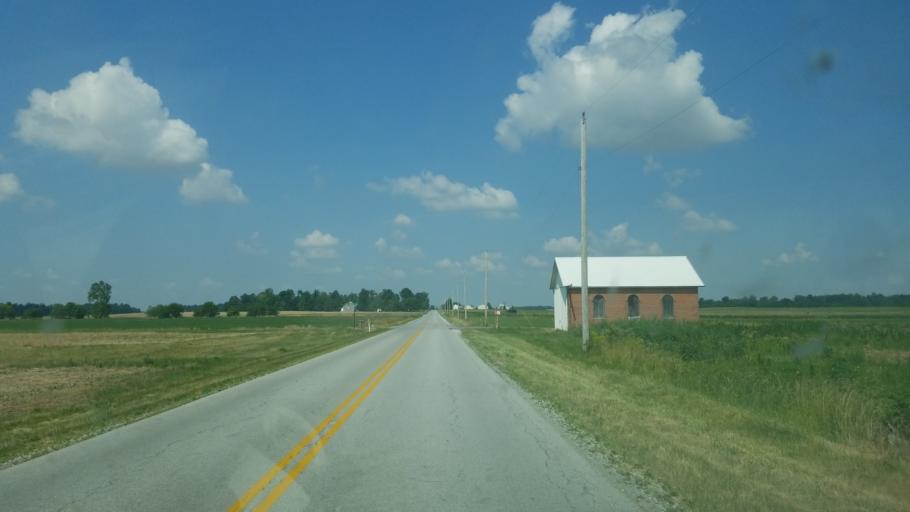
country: US
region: Ohio
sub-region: Auglaize County
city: Wapakoneta
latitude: 40.5705
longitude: -84.1255
